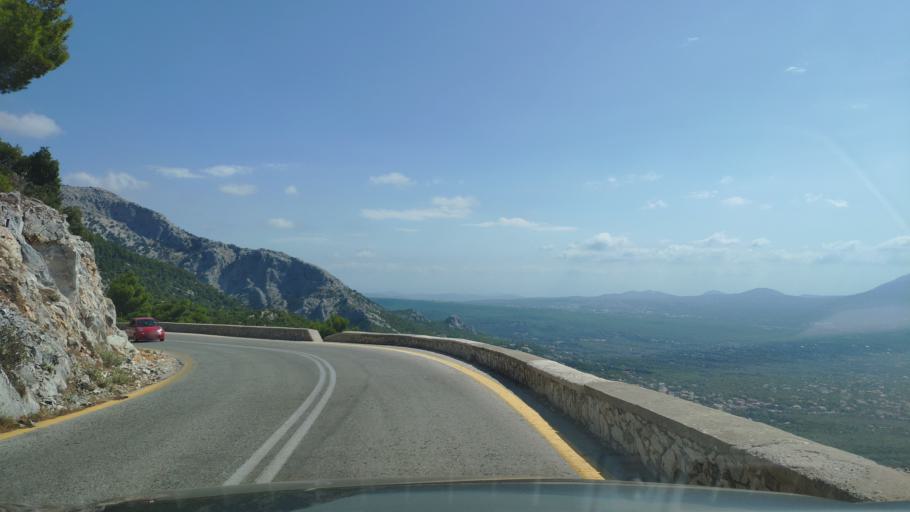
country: GR
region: Attica
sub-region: Nomarchia Anatolikis Attikis
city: Thrakomakedones
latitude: 38.1419
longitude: 23.7271
